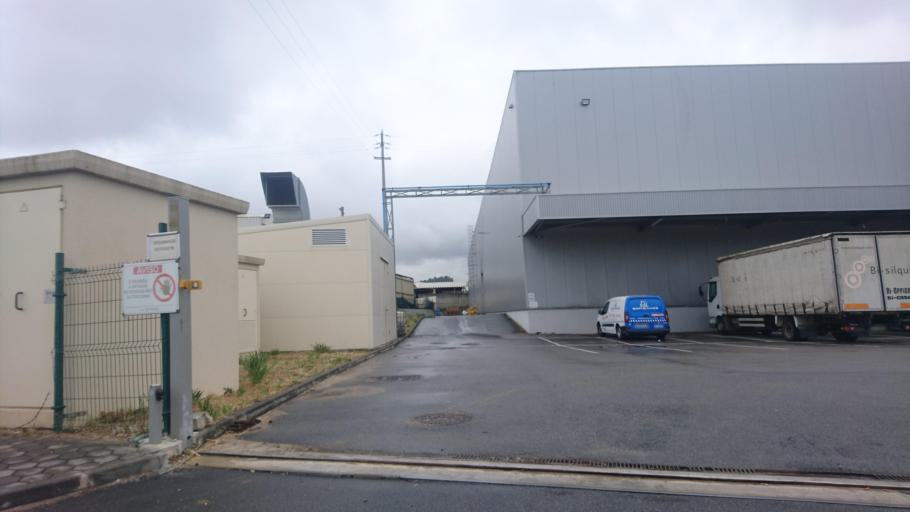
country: PT
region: Aveiro
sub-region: Ovar
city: Esmoriz
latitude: 40.9653
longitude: -8.6354
